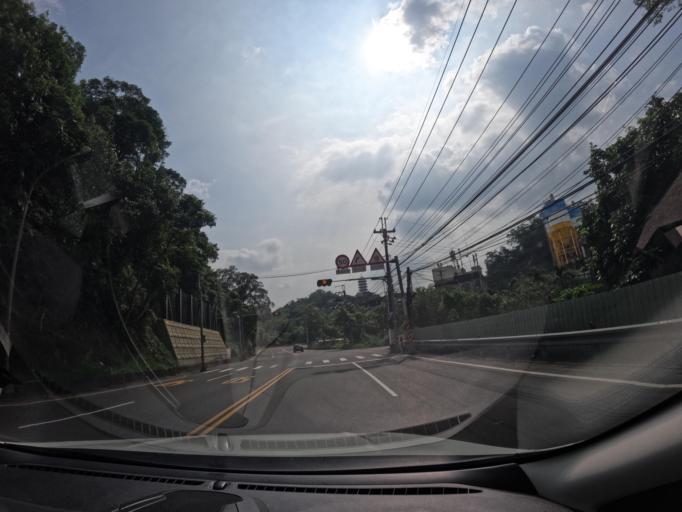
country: TW
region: Taiwan
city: Daxi
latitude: 24.9033
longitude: 121.3507
